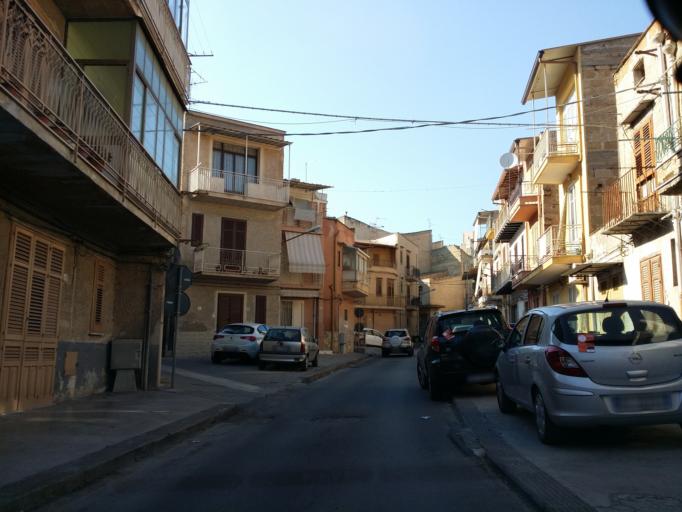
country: IT
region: Sicily
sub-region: Palermo
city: Misilmeri
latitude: 38.0302
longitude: 13.4479
